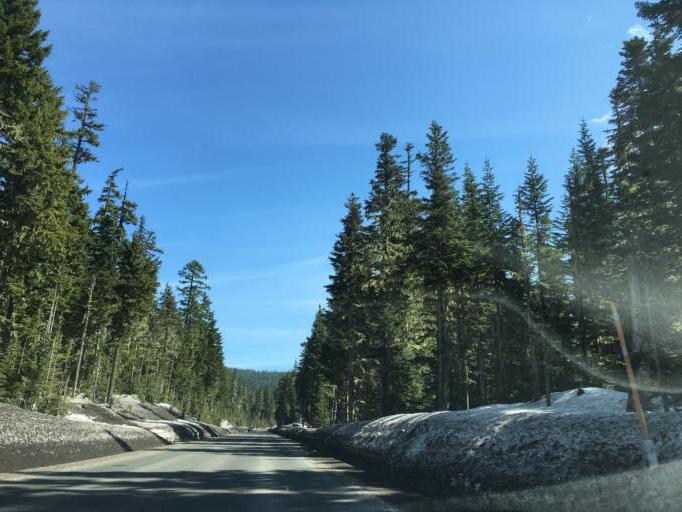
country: US
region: Oregon
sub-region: Clackamas County
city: Mount Hood Village
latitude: 45.3022
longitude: -121.7256
